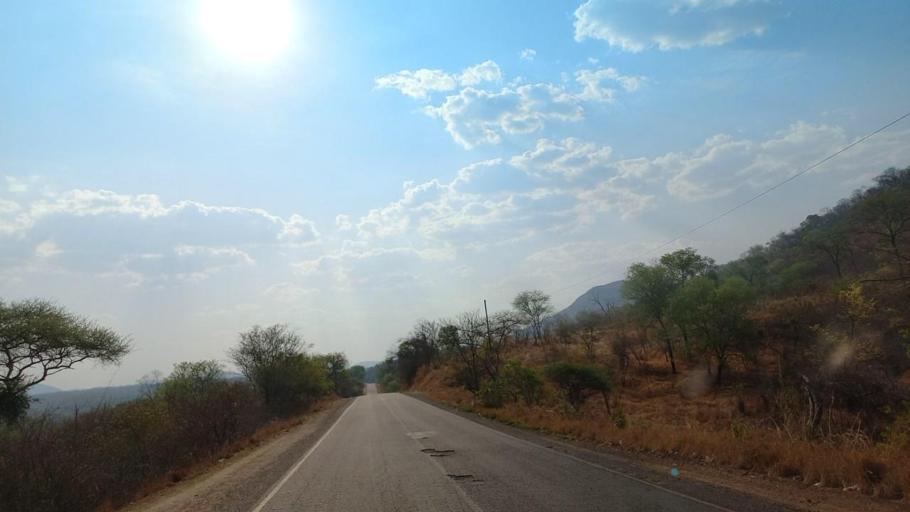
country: ZM
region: Lusaka
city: Luangwa
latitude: -14.9825
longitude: 30.1730
